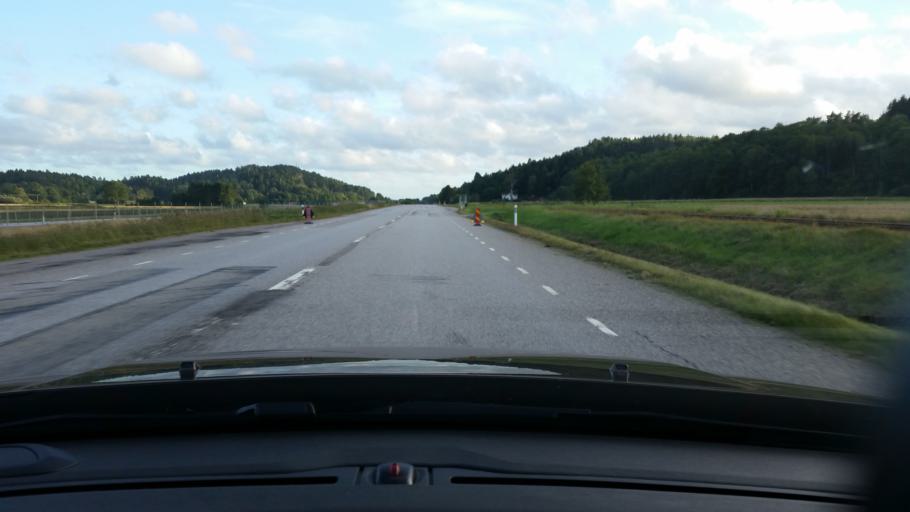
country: SE
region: Vaestra Goetaland
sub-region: Lilla Edets Kommun
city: Lodose
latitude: 58.0799
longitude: 12.1551
